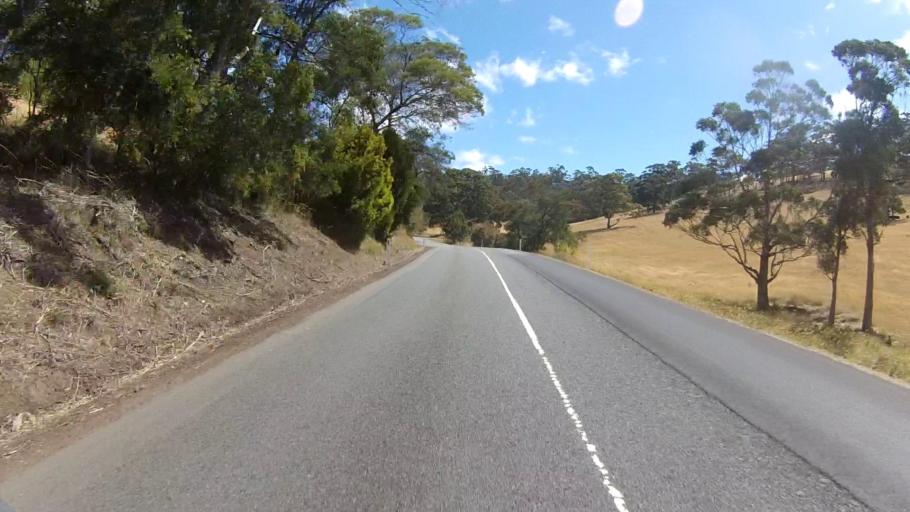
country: AU
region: Tasmania
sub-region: Sorell
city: Sorell
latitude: -42.7386
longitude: 147.4828
